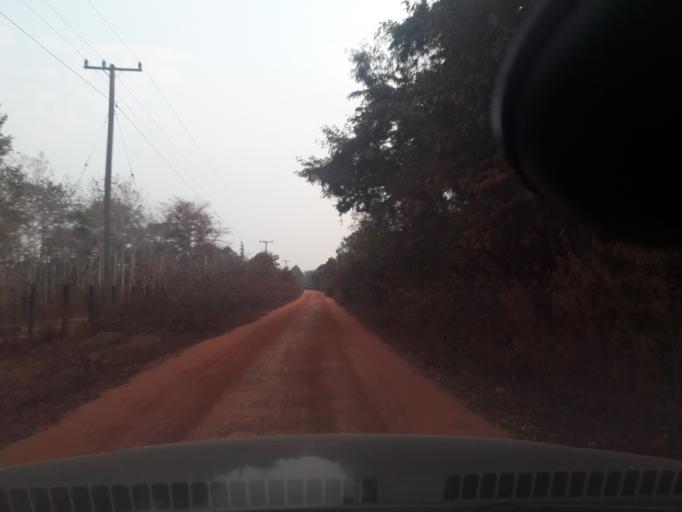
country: TH
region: Nong Khai
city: Si Chiang Mai
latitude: 18.0514
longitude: 102.4884
